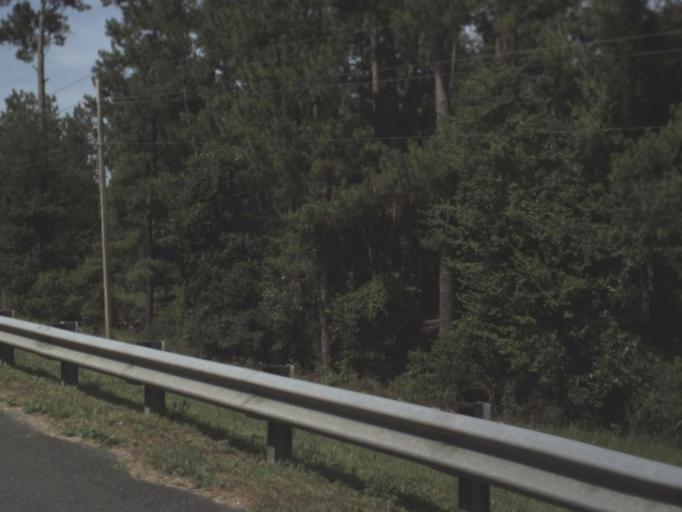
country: US
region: Florida
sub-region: Lafayette County
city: Mayo
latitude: 30.1156
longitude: -83.1703
